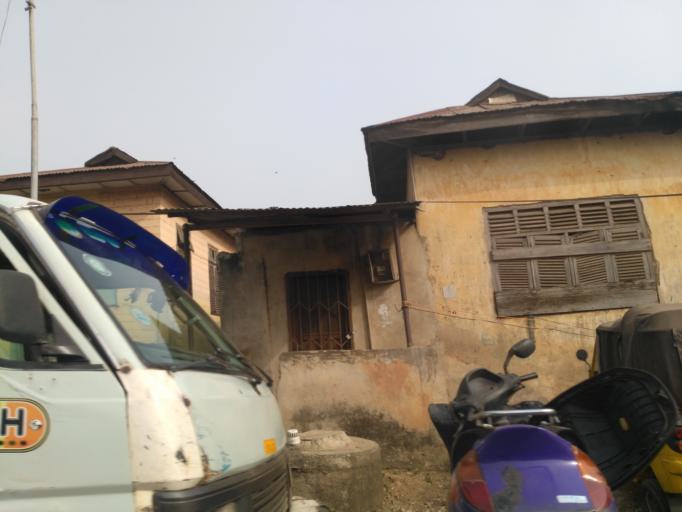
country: GH
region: Ashanti
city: Kumasi
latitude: 6.6977
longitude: -1.6122
